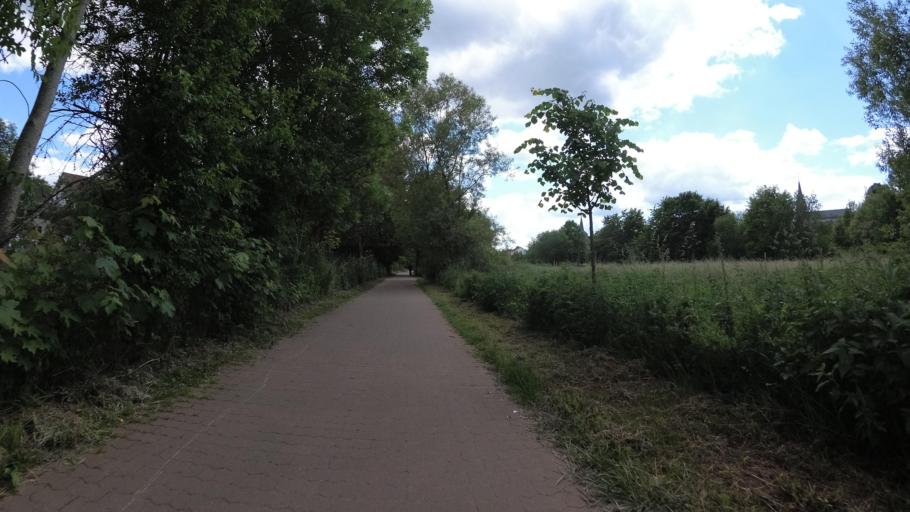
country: DE
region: Saarland
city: Puttlingen
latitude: 49.3044
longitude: 6.8991
